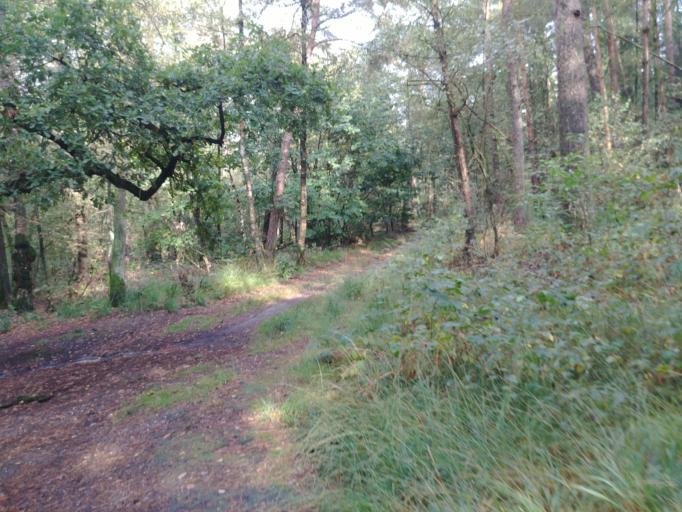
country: NL
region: Gelderland
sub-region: Gemeente Renkum
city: Wolfheze
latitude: 51.9970
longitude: 5.8134
